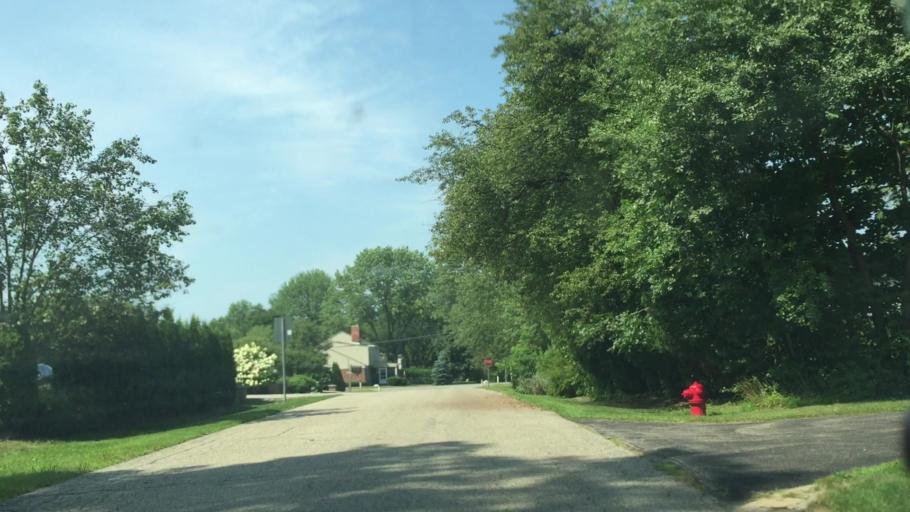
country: US
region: Michigan
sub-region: Oakland County
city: Franklin
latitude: 42.5513
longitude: -83.3087
